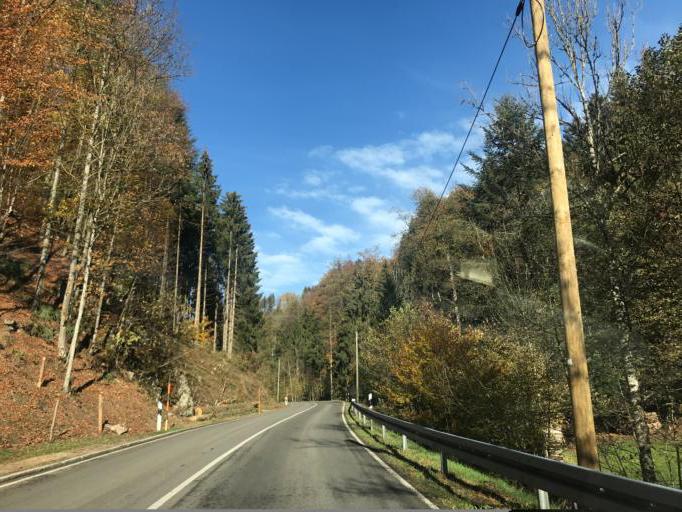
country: DE
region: Baden-Wuerttemberg
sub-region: Freiburg Region
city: Sankt Peter
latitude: 48.0232
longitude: 8.0267
